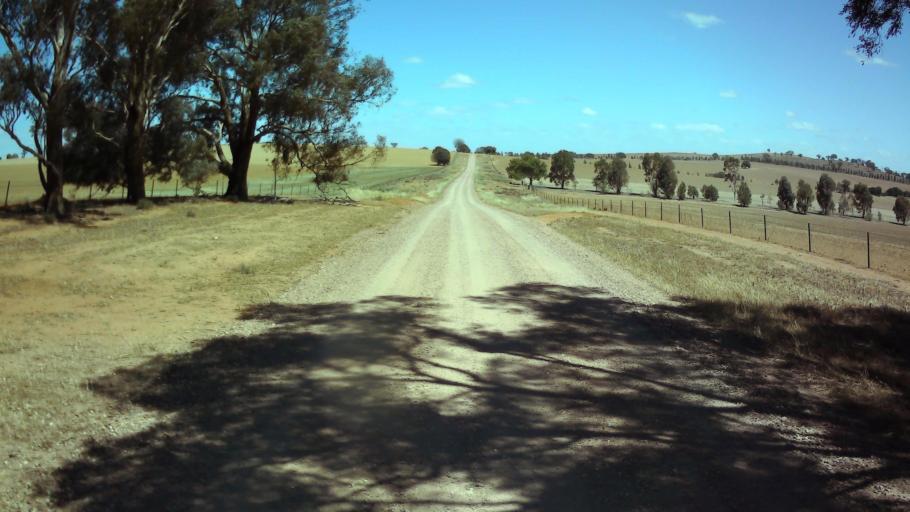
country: AU
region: New South Wales
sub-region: Weddin
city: Grenfell
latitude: -33.9425
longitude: 148.3298
